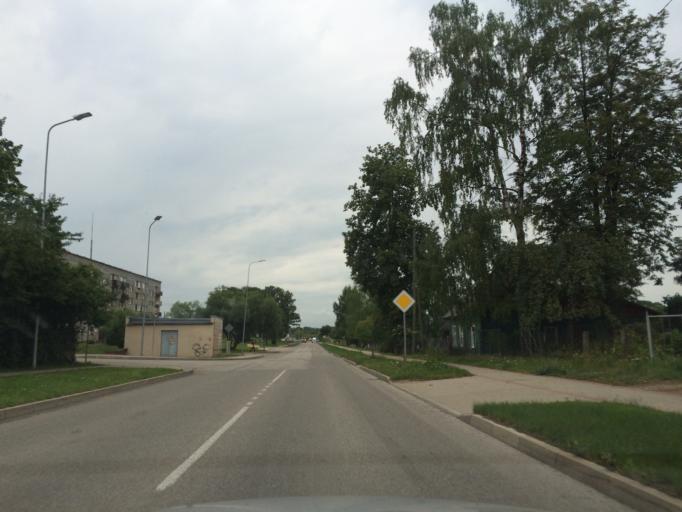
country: LV
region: Rezekne
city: Rezekne
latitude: 56.5155
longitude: 27.3296
